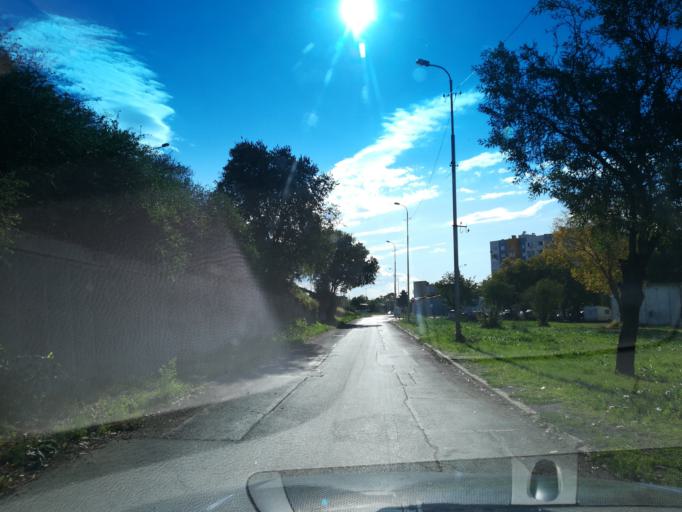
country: BG
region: Stara Zagora
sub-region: Obshtina Stara Zagora
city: Stara Zagora
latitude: 42.4256
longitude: 25.6465
